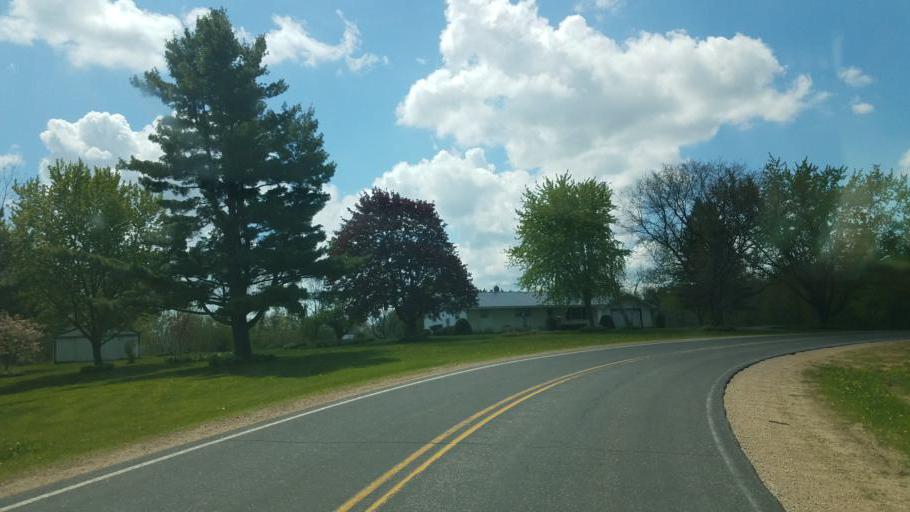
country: US
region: Wisconsin
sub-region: Vernon County
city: Hillsboro
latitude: 43.6789
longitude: -90.3484
